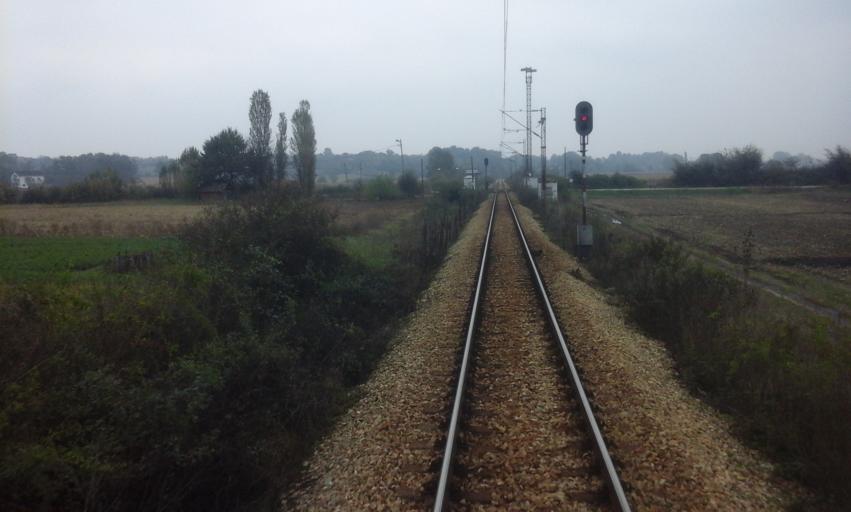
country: RS
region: Central Serbia
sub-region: Belgrade
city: Mladenovac
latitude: 44.3847
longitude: 20.7728
